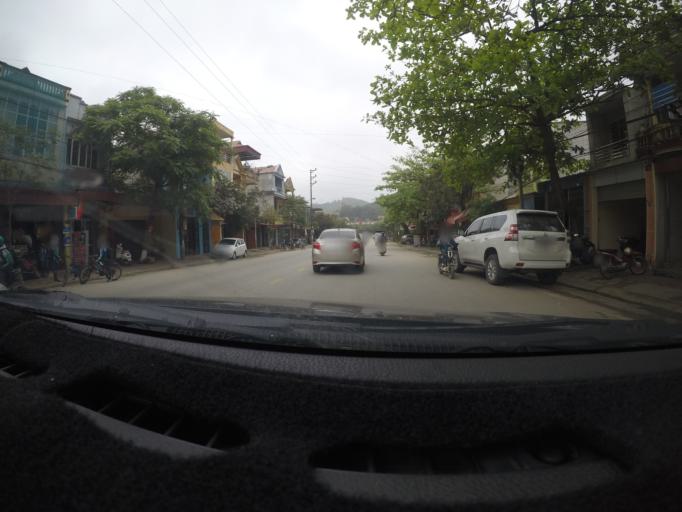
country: VN
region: Yen Bai
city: Yen Bai
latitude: 21.7306
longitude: 104.9604
